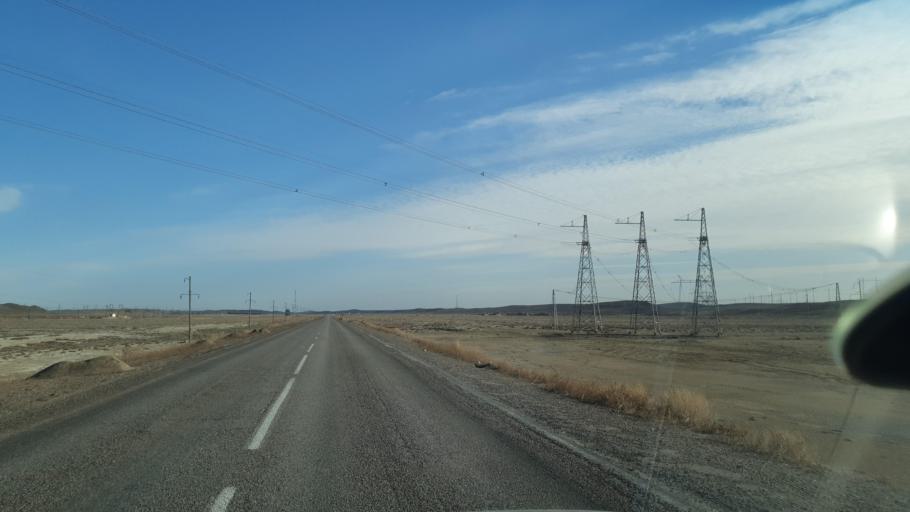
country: KZ
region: Zhambyl
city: Mynaral
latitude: 45.5616
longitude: 73.4293
